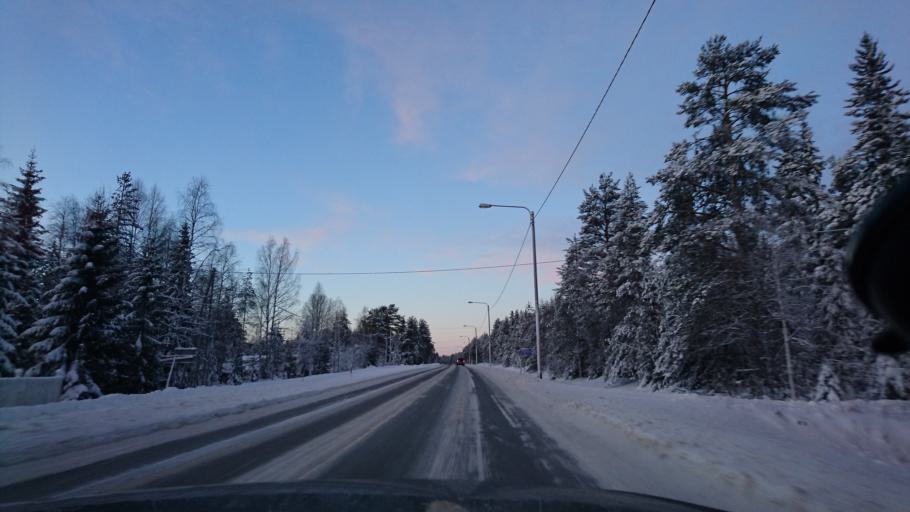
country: FI
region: Lapland
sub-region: Rovaniemi
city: Ranua
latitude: 65.9393
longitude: 26.4844
